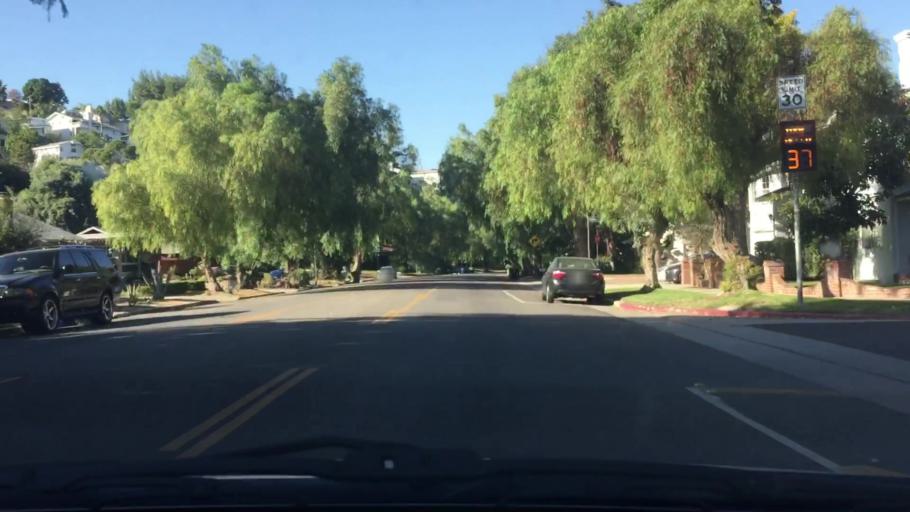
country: US
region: California
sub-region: Los Angeles County
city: Woodland Hills
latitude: 34.1621
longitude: -118.5969
